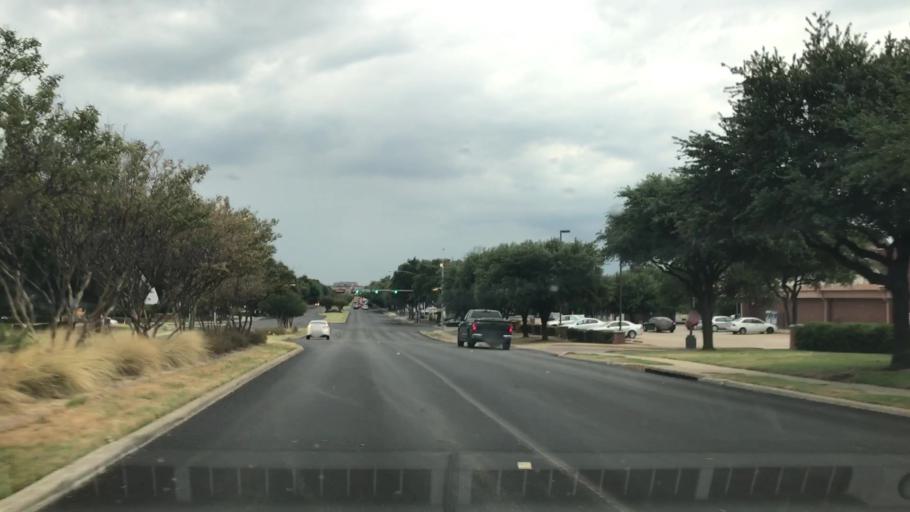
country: US
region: Texas
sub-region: Dallas County
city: Farmers Branch
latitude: 32.9417
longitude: -96.9521
